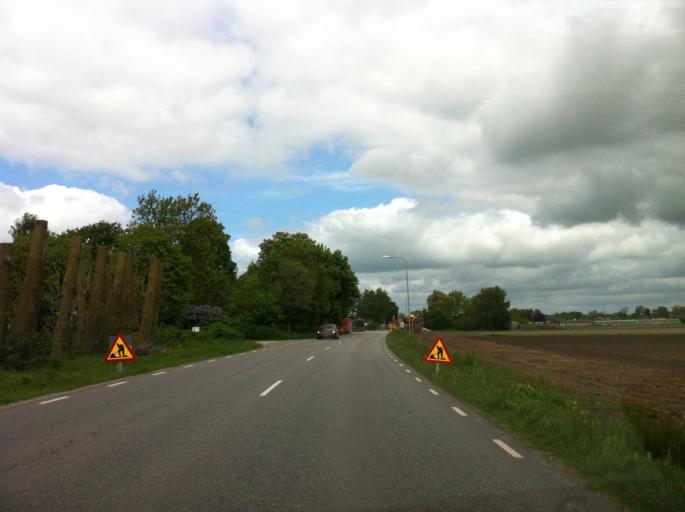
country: SE
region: Skane
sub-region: Svalovs Kommun
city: Teckomatorp
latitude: 55.8365
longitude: 13.0984
